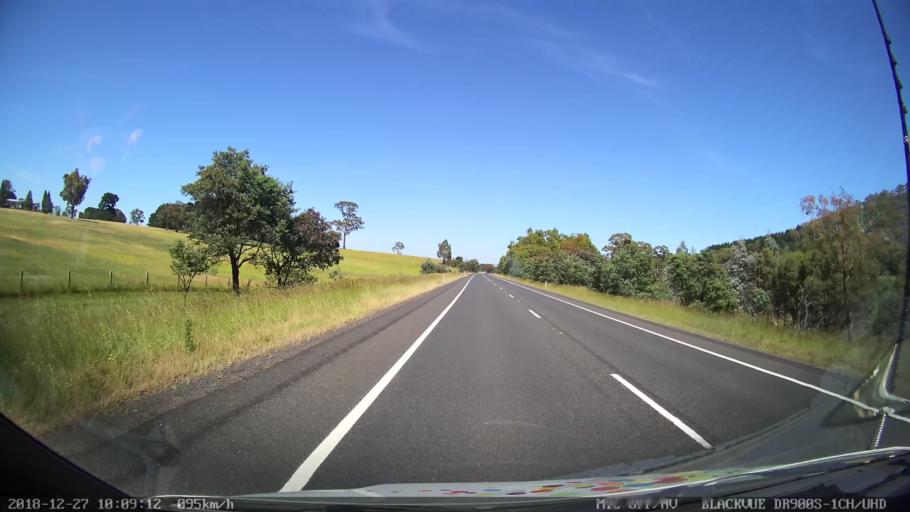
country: AU
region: New South Wales
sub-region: Lithgow
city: Portland
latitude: -33.4504
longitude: 149.8131
